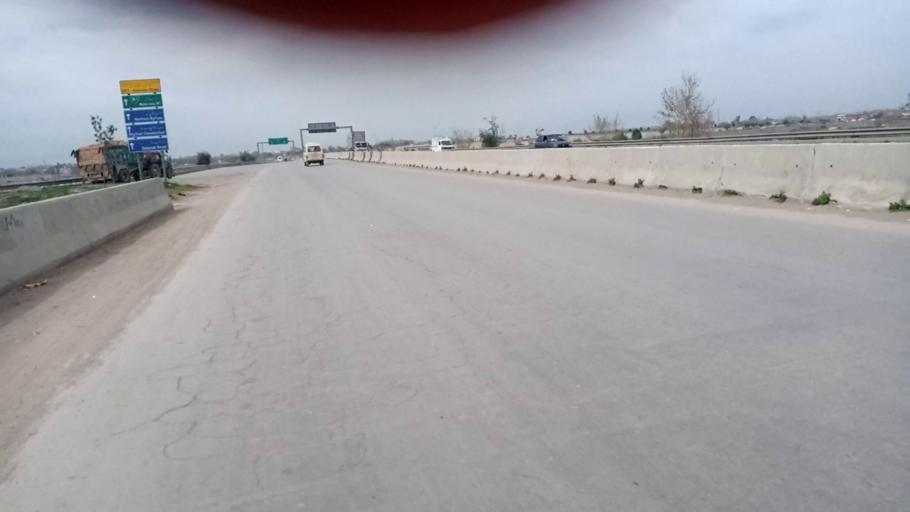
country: PK
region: Khyber Pakhtunkhwa
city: Peshawar
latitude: 34.0201
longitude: 71.6477
